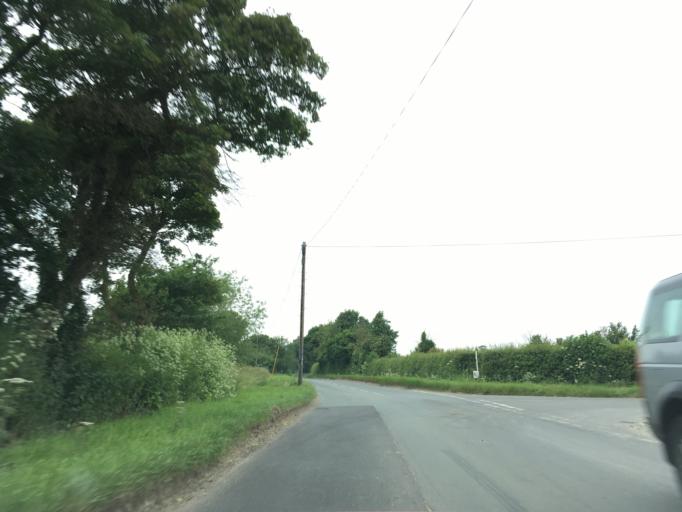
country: GB
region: England
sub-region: Gloucestershire
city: Stonehouse
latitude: 51.7613
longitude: -2.3431
